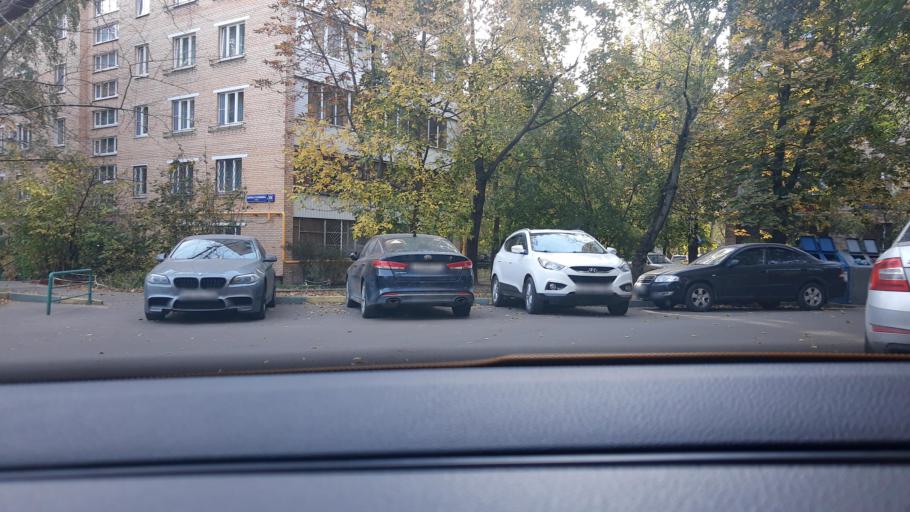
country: RU
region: Moscow
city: Rostokino
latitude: 55.8224
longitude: 37.6542
